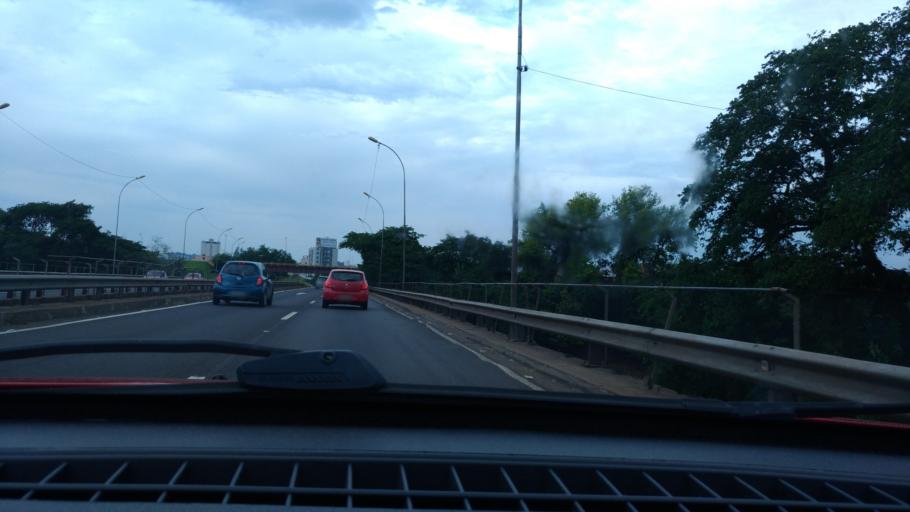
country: BR
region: Rio Grande do Sul
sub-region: Sao Leopoldo
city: Sao Leopoldo
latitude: -29.7586
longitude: -51.1521
